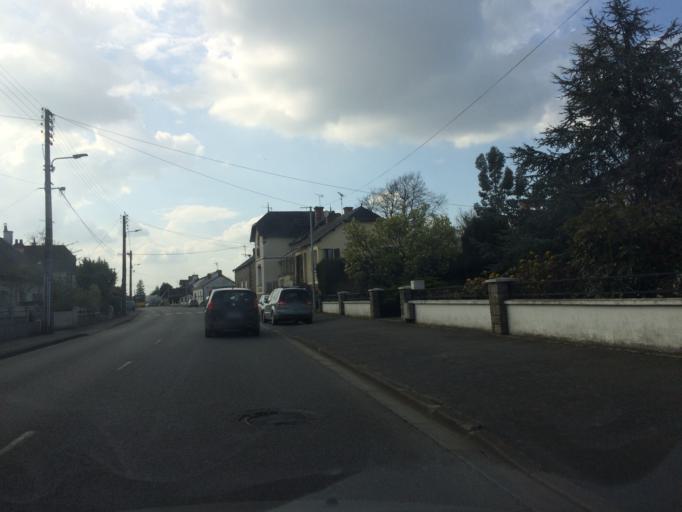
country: FR
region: Pays de la Loire
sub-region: Departement de la Loire-Atlantique
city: Blain
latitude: 47.4778
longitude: -1.7698
